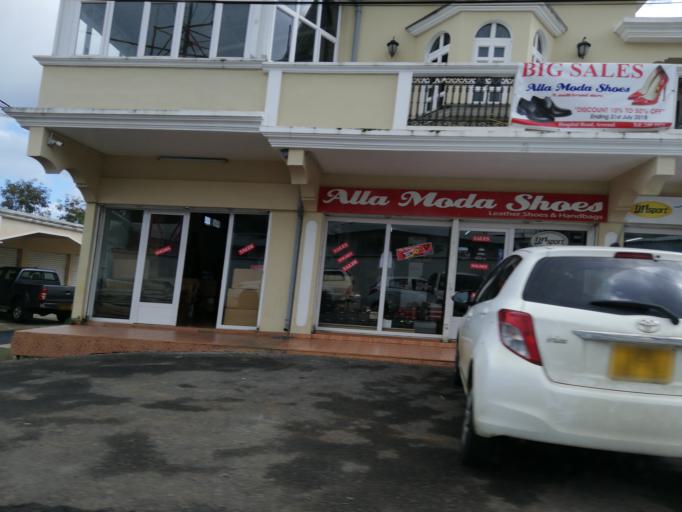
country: MU
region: Pamplemousses
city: Arsenal
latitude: -20.1035
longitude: 57.5430
